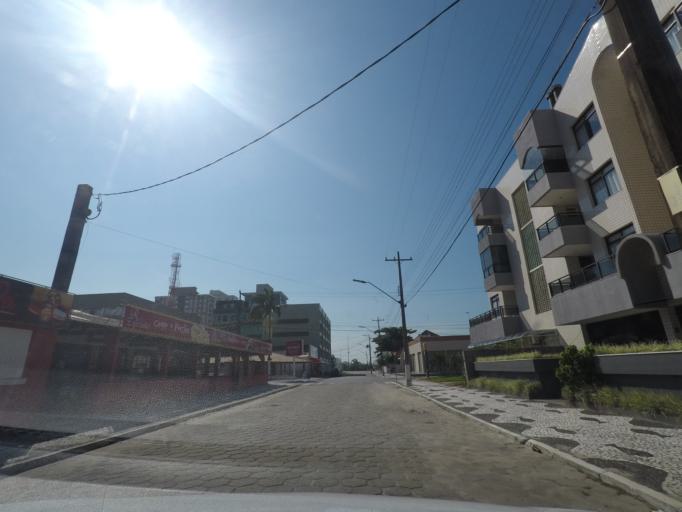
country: BR
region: Parana
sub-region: Guaratuba
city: Guaratuba
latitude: -25.8458
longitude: -48.5392
